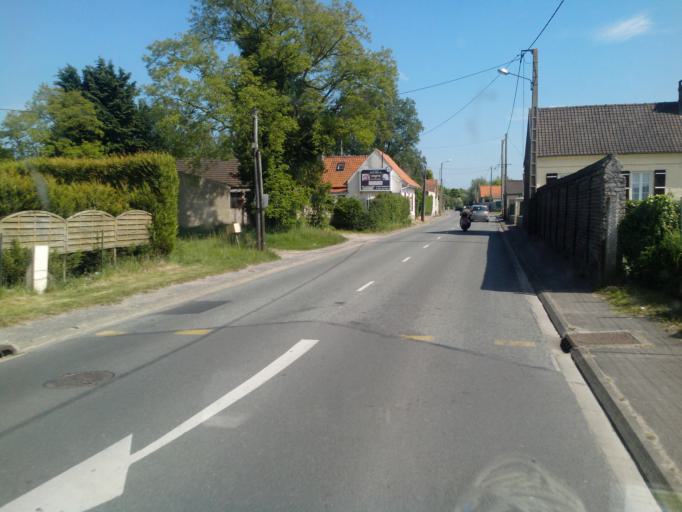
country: FR
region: Nord-Pas-de-Calais
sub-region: Departement du Pas-de-Calais
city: Verton
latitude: 50.3774
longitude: 1.6561
